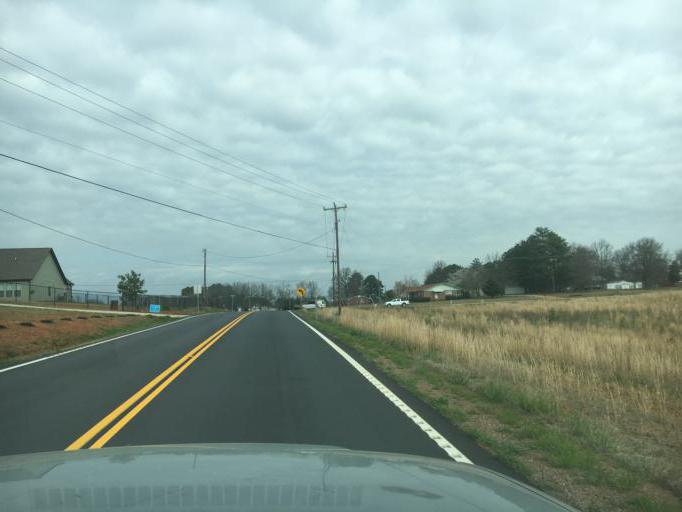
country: US
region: South Carolina
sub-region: Spartanburg County
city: Inman Mills
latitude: 35.0489
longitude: -82.1382
